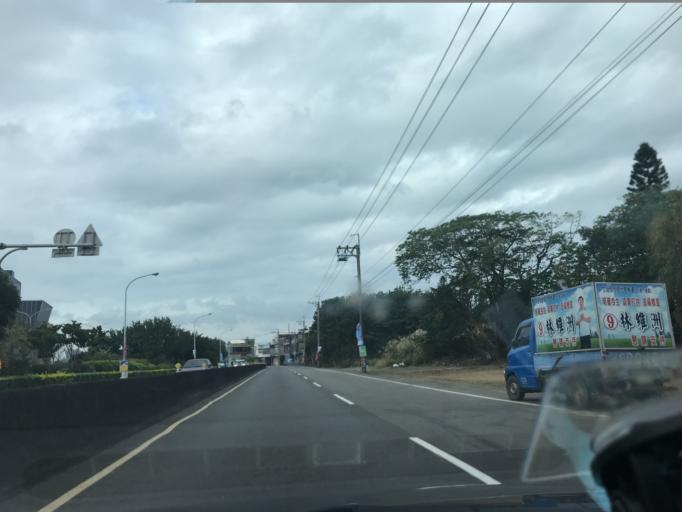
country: TW
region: Taiwan
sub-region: Hsinchu
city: Zhubei
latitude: 24.8057
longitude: 121.0491
